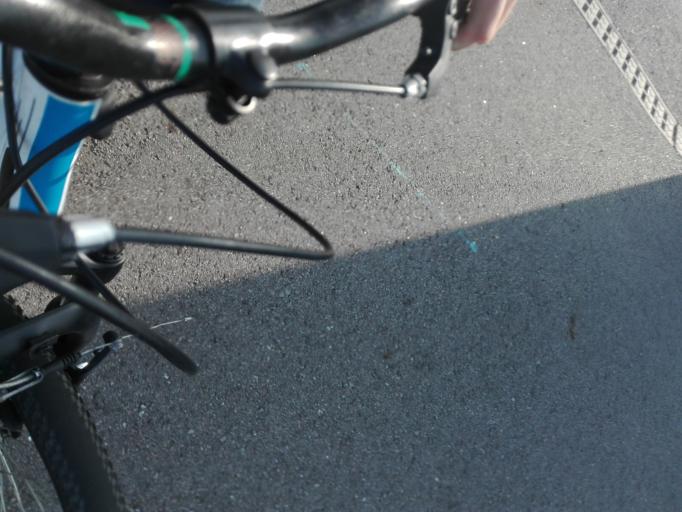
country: RU
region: Krasnodarskiy
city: Adler
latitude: 43.4106
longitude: 39.9720
